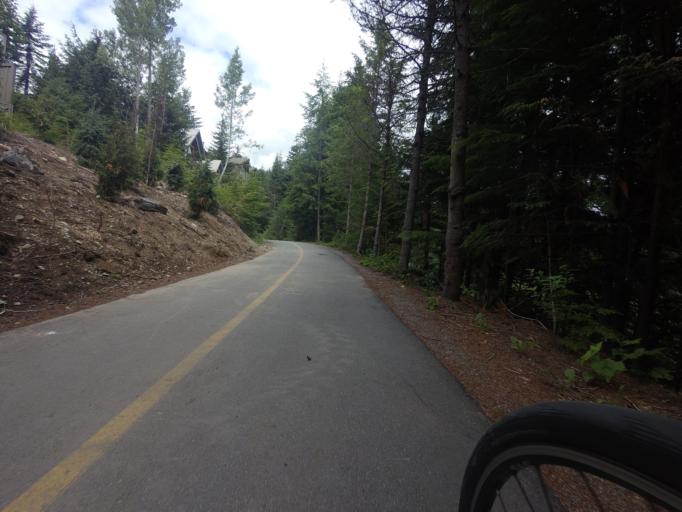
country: CA
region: British Columbia
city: Whistler
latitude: 50.1127
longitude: -122.9669
